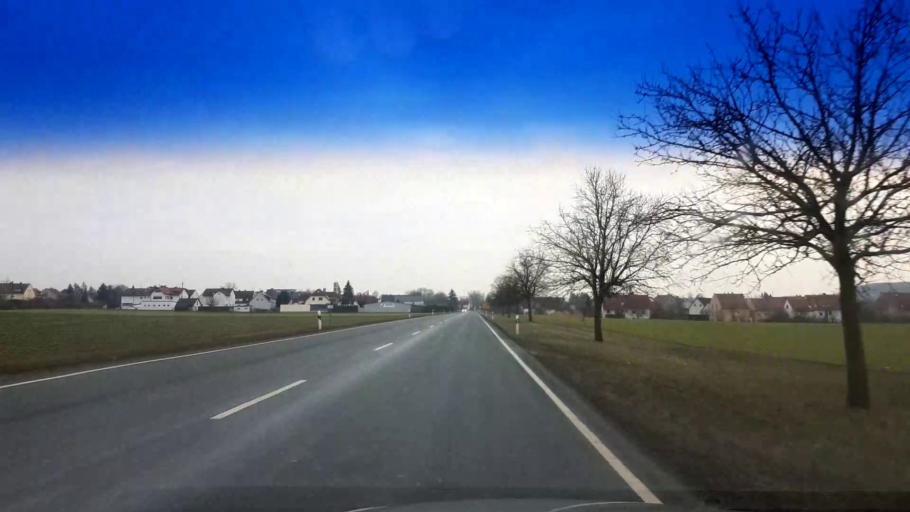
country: DE
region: Bavaria
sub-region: Upper Franconia
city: Altendorf
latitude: 49.8043
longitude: 11.0071
